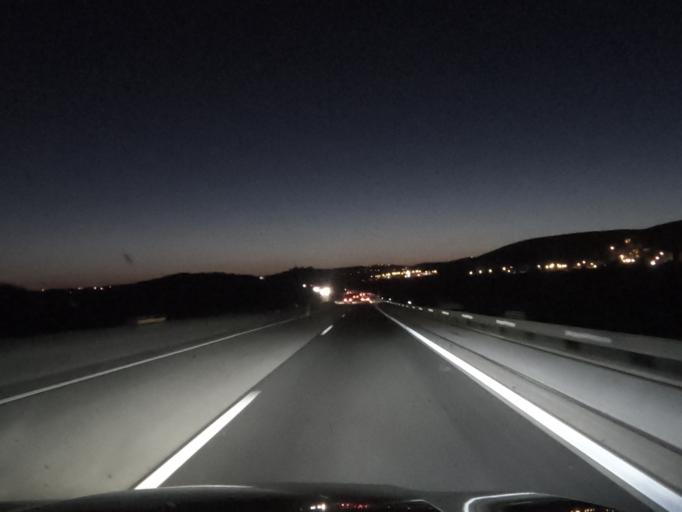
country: PT
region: Faro
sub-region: Loule
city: Vilamoura
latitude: 37.1268
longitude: -8.0903
